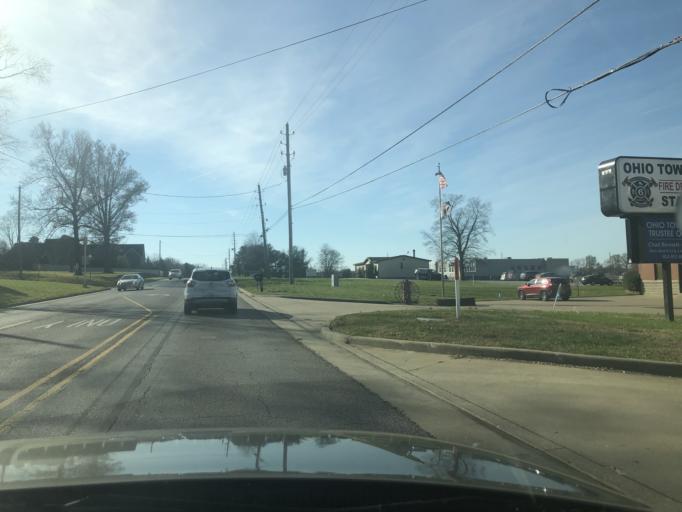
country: US
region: Indiana
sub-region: Warrick County
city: Newburgh
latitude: 37.9731
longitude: -87.4412
